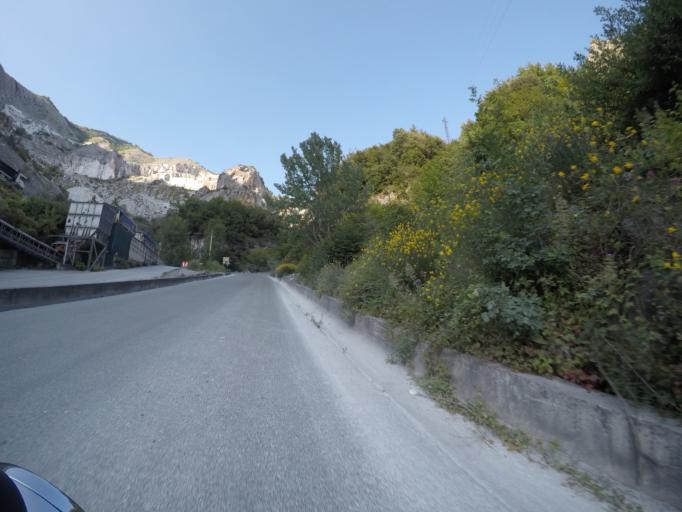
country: IT
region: Tuscany
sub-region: Provincia di Massa-Carrara
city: Carrara
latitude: 44.0994
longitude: 10.1205
